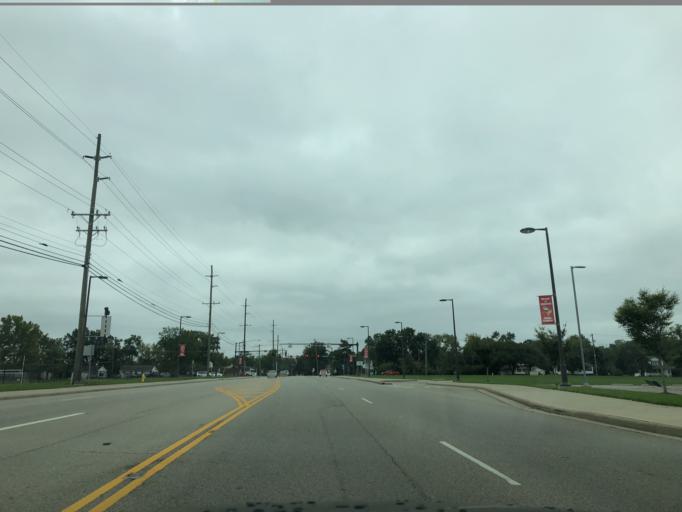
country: US
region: Ohio
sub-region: Hamilton County
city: Glendale
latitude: 39.2725
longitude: -84.4444
